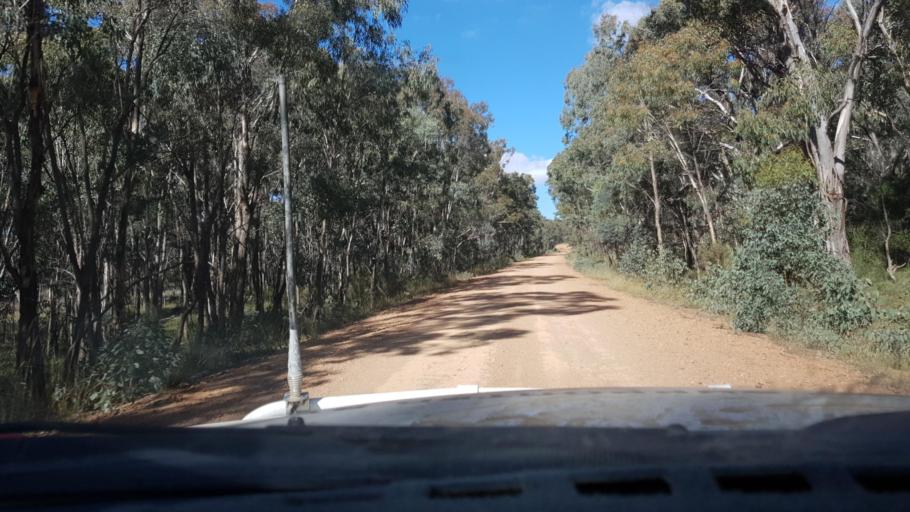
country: AU
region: New South Wales
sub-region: Tamworth Municipality
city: Manilla
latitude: -30.4499
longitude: 150.8759
